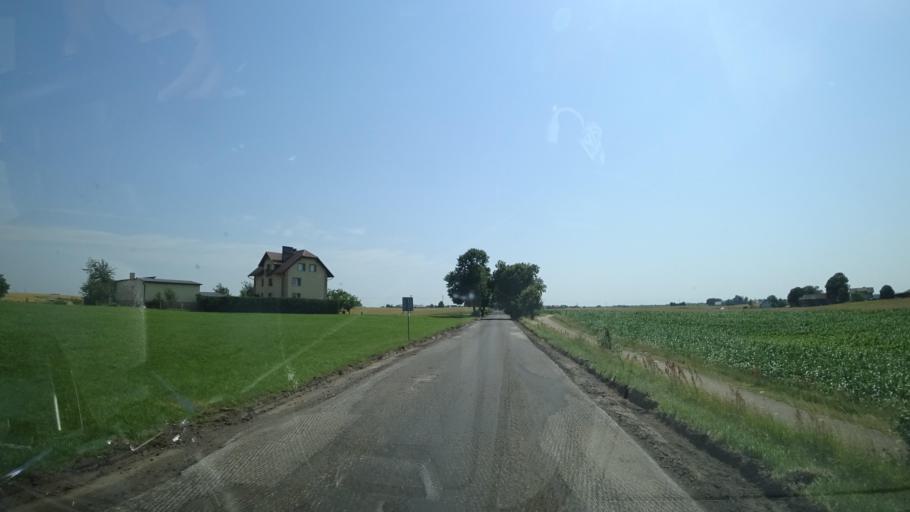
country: PL
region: Pomeranian Voivodeship
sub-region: Powiat chojnicki
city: Brusy
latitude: 53.8742
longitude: 17.6607
